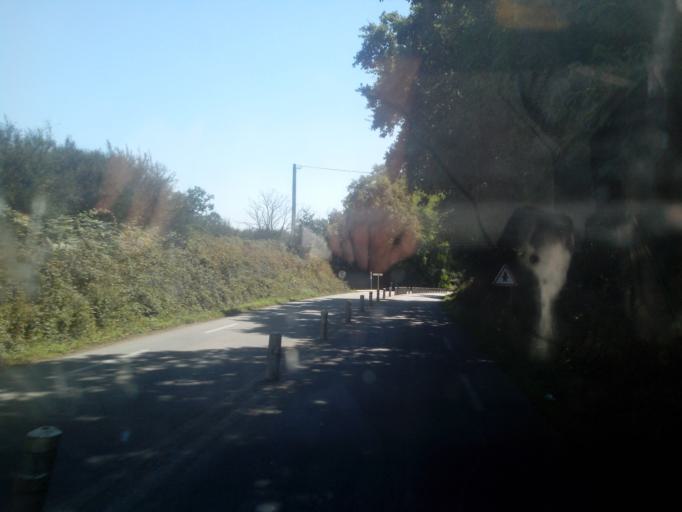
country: FR
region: Brittany
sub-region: Departement du Morbihan
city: Josselin
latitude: 47.9443
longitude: -2.5439
